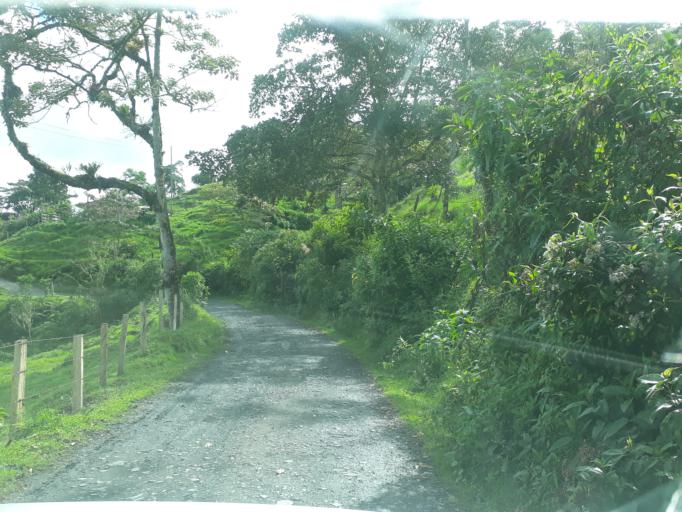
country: CO
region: Cundinamarca
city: Carmen de Carupa
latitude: 5.3374
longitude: -74.0557
